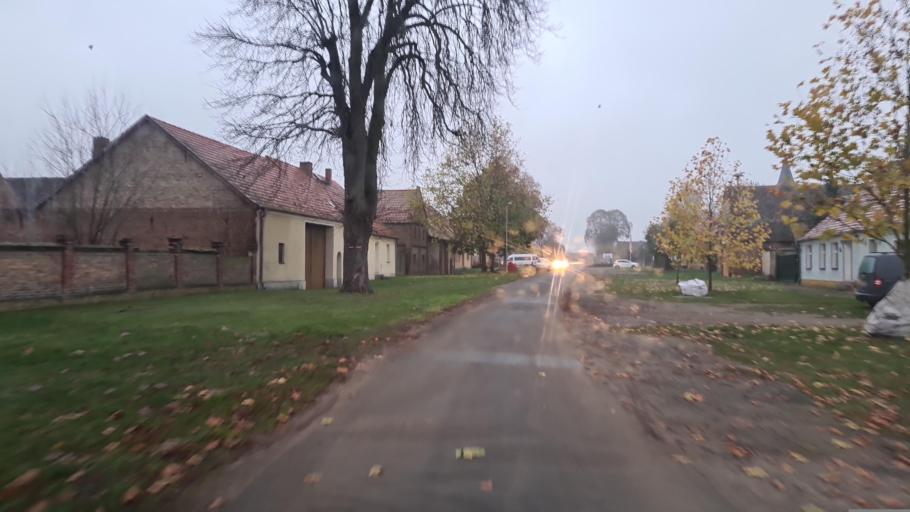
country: DE
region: Brandenburg
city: Beelitz
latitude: 52.2419
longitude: 13.0203
